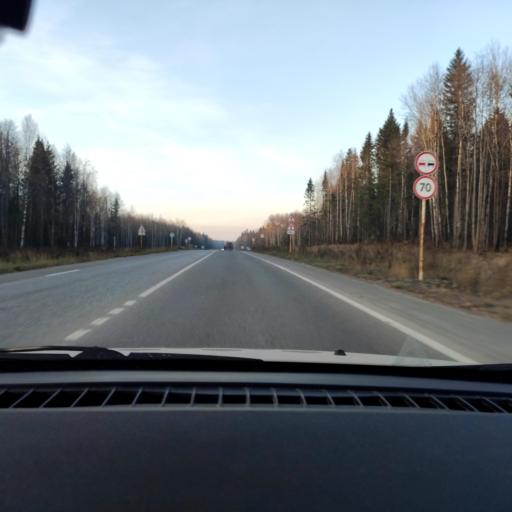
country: RU
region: Perm
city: Novyye Lyady
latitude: 58.0479
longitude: 56.5478
